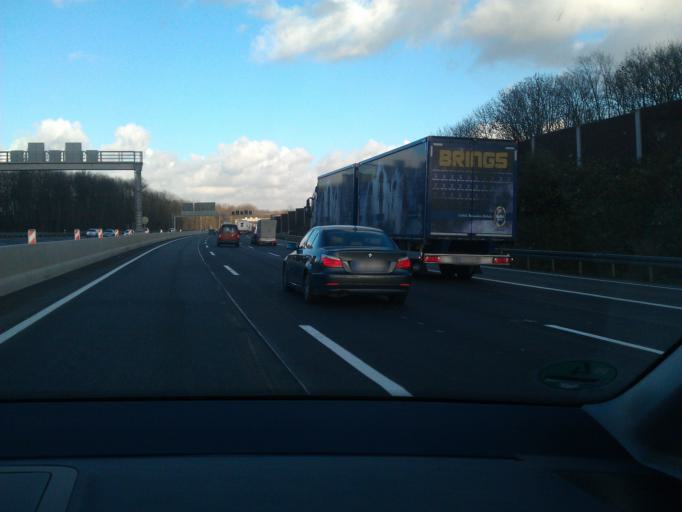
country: DE
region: North Rhine-Westphalia
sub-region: Regierungsbezirk Koln
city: Mengenich
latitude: 50.9803
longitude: 6.8524
